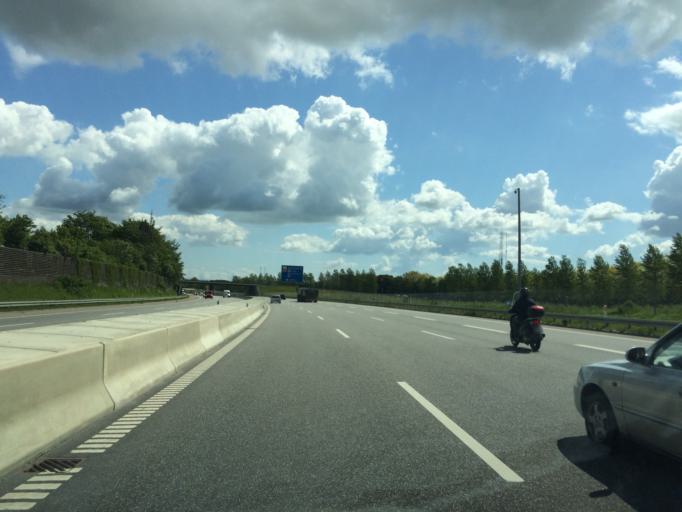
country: DK
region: Zealand
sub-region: Roskilde Kommune
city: Roskilde
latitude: 55.6234
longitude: 12.0740
